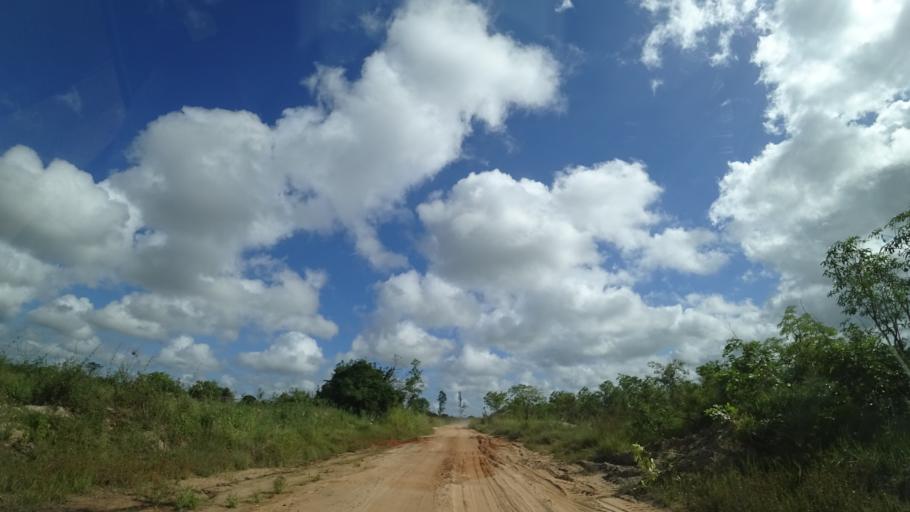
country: MZ
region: Sofala
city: Dondo
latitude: -19.4309
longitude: 34.7096
